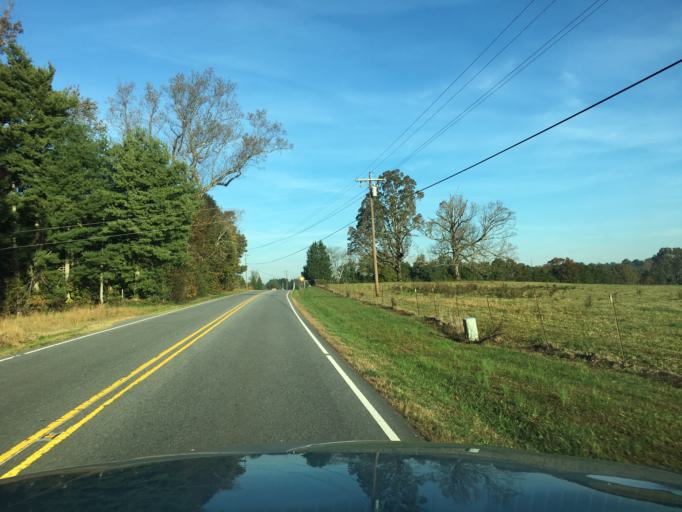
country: US
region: North Carolina
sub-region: Catawba County
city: Newton
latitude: 35.6245
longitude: -81.2625
